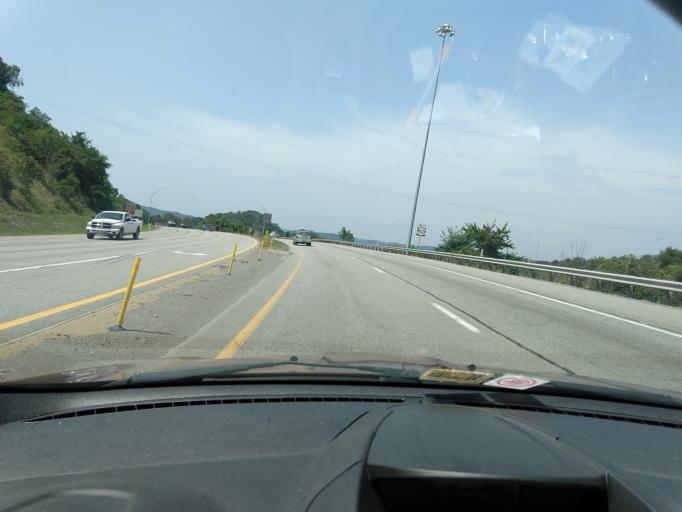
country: US
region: West Virginia
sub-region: Harrison County
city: Despard
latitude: 39.2765
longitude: -80.3008
